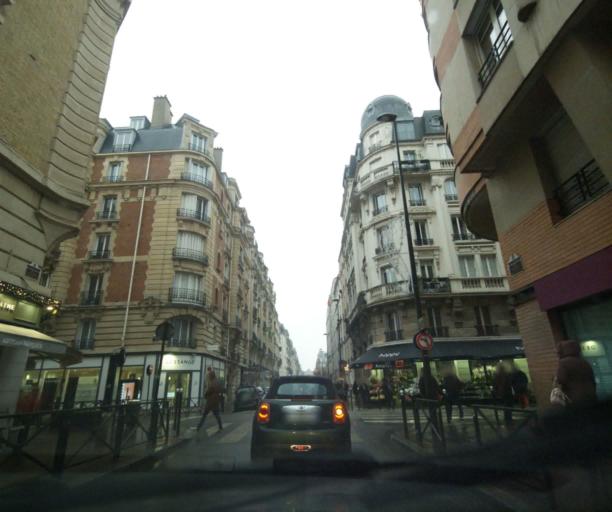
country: FR
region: Ile-de-France
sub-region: Departement des Hauts-de-Seine
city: Levallois-Perret
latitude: 48.8926
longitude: 2.2857
